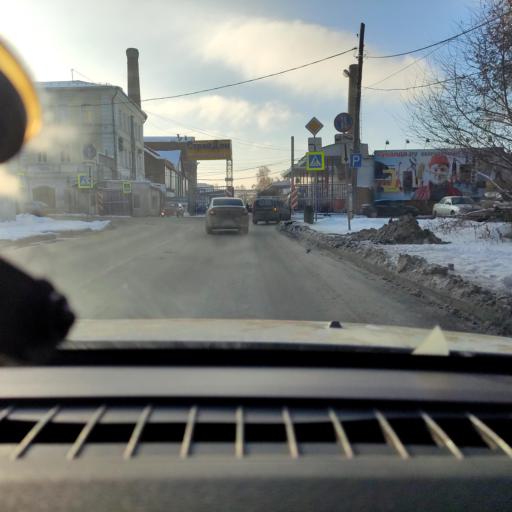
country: RU
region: Samara
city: Rozhdestveno
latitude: 53.1809
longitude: 50.0751
